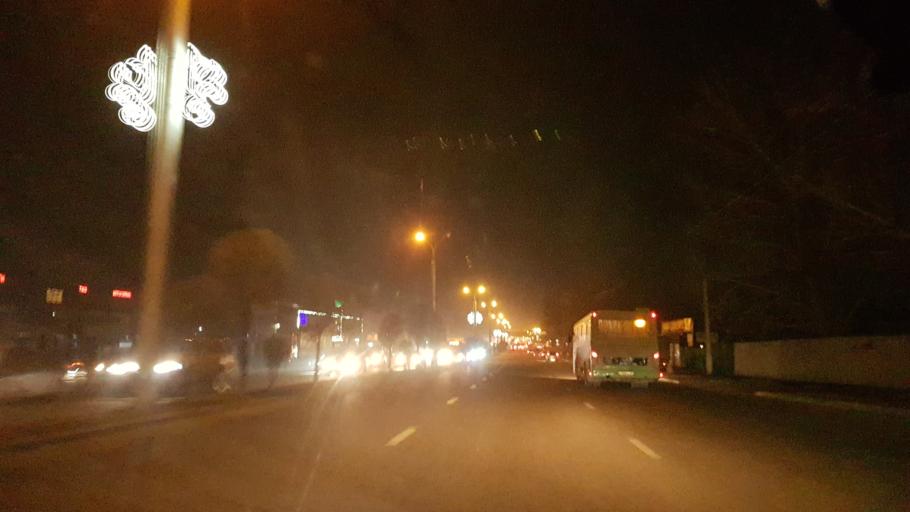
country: KZ
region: Almaty Qalasy
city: Almaty
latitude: 43.2610
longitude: 76.8543
